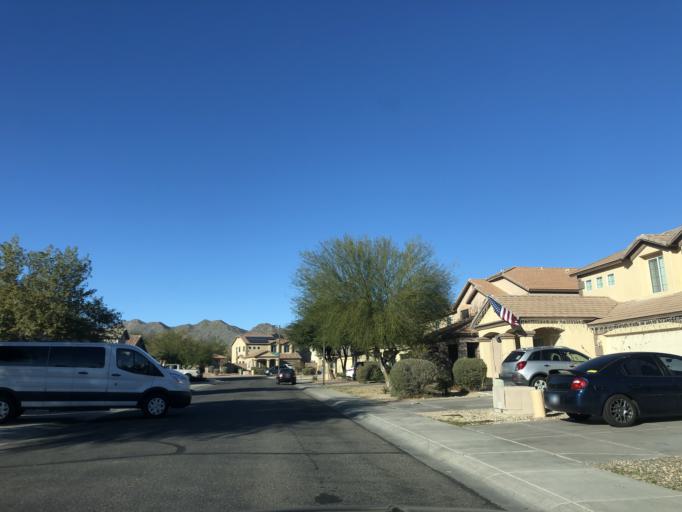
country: US
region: Arizona
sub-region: Maricopa County
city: Buckeye
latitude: 33.4376
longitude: -112.5723
